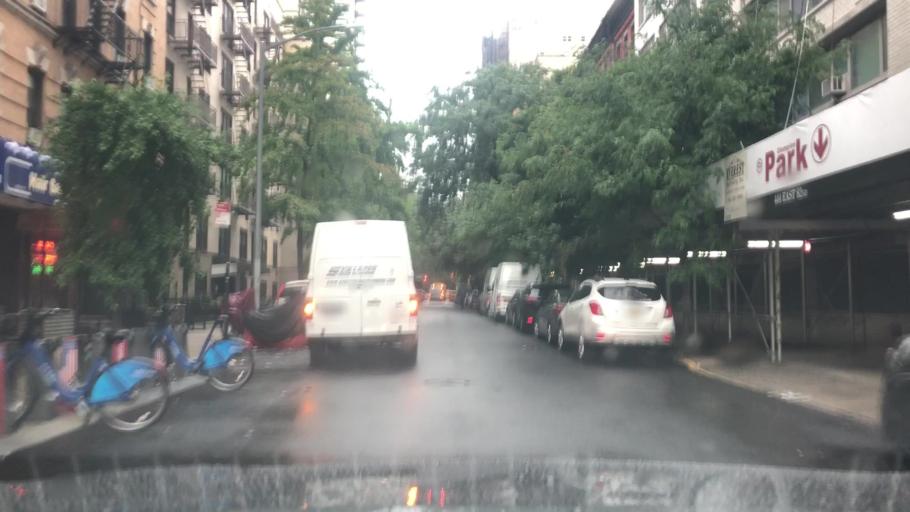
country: US
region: New York
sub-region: New York County
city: Manhattan
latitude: 40.7729
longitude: -73.9498
